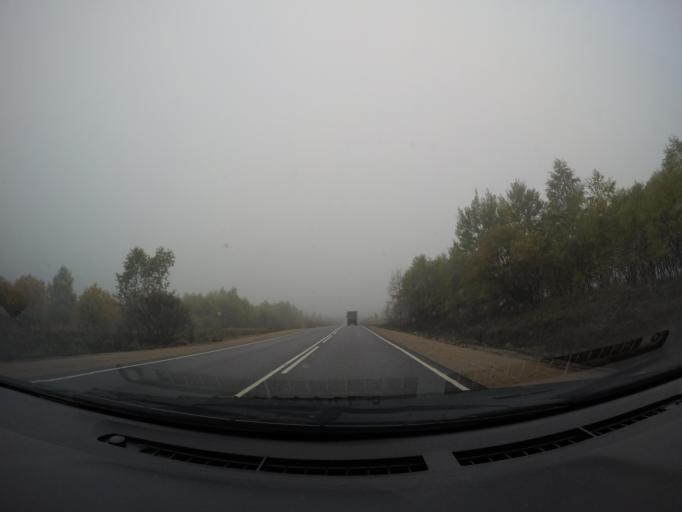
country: RU
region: Moskovskaya
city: Novopetrovskoye
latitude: 55.8384
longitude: 36.4564
